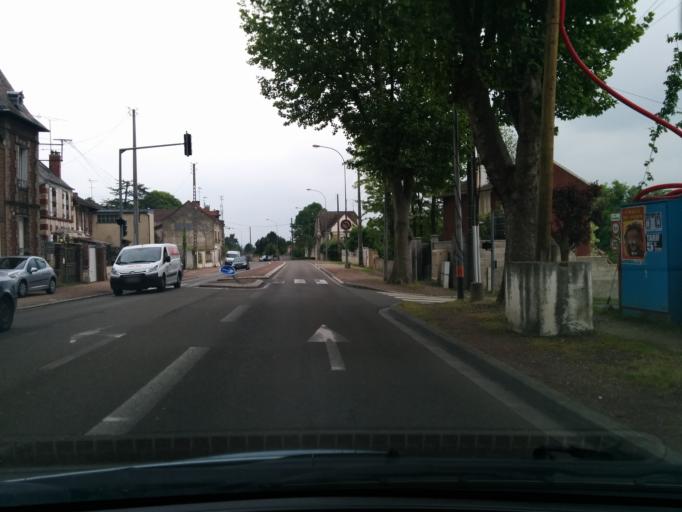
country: FR
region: Ile-de-France
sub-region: Departement des Yvelines
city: Juziers
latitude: 48.9896
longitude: 1.8427
